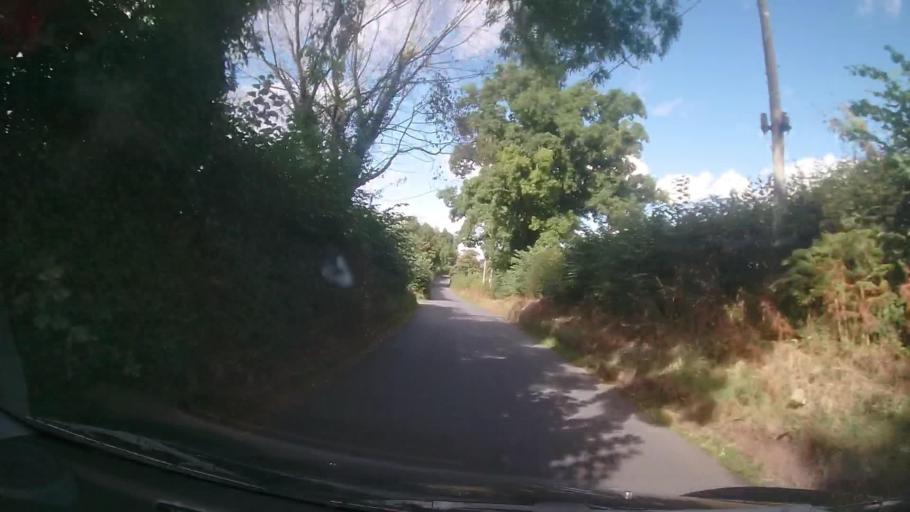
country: GB
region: Wales
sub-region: Sir Powys
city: Brecon
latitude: 51.8895
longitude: -3.3005
